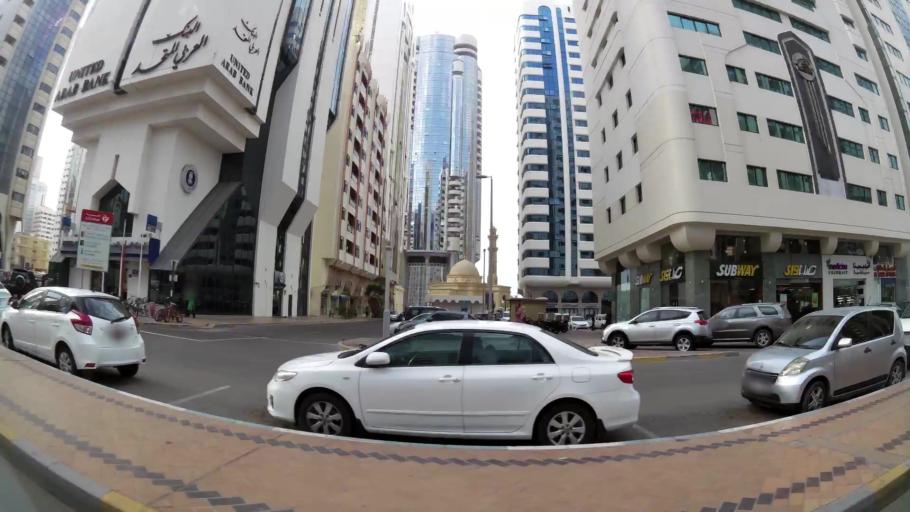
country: AE
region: Abu Dhabi
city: Abu Dhabi
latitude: 24.4912
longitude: 54.3601
